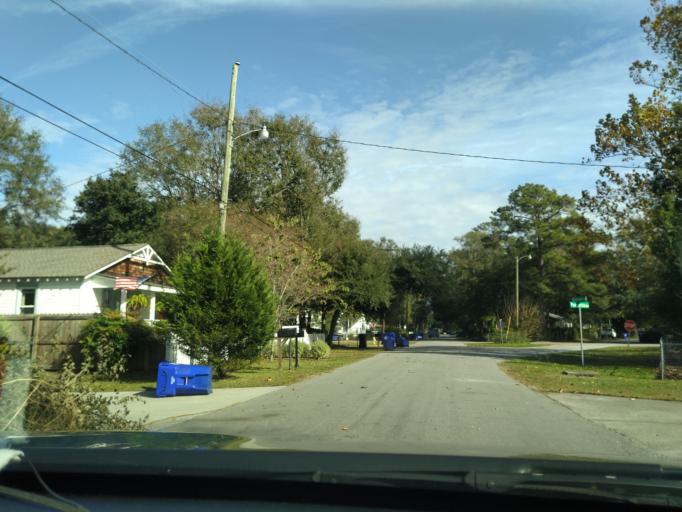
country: US
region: South Carolina
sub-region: Charleston County
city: North Charleston
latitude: 32.8024
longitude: -80.0126
